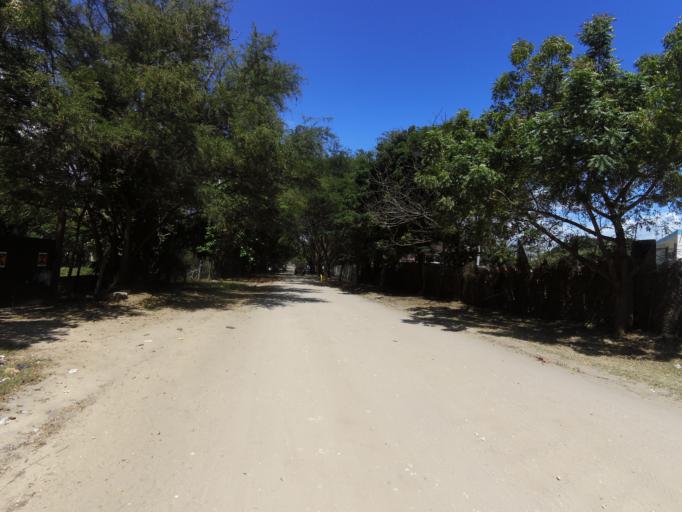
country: TZ
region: Dar es Salaam
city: Magomeni
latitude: -6.7935
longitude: 39.2724
